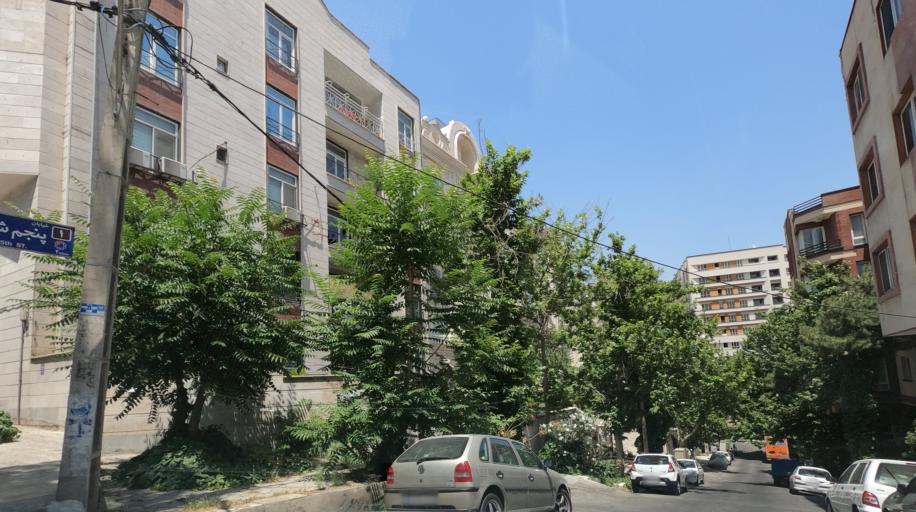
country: IR
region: Tehran
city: Tajrish
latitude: 35.7872
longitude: 51.3838
